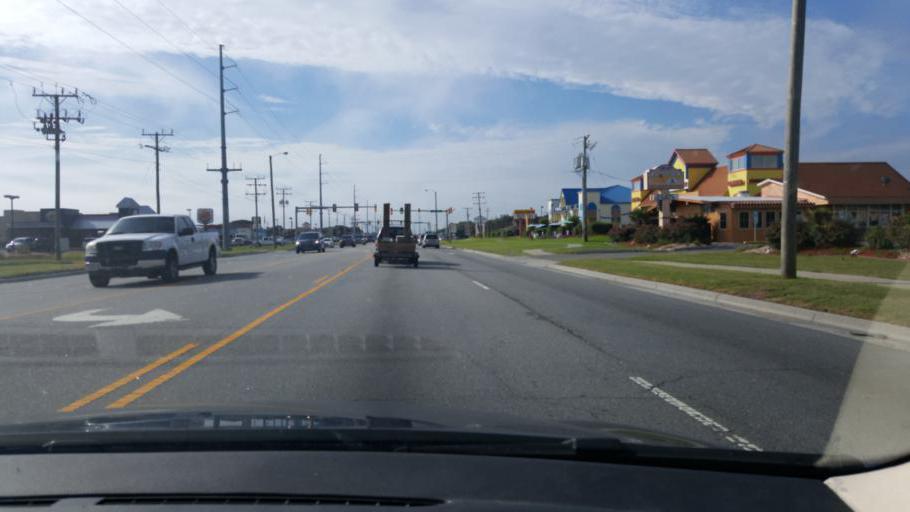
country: US
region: North Carolina
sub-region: Dare County
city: Kill Devil Hills
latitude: 35.9996
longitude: -75.6526
